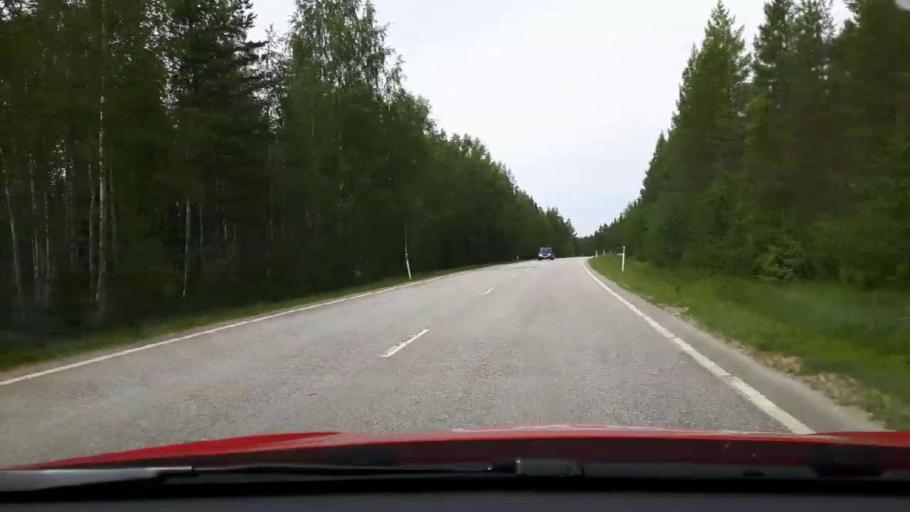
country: SE
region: Jaemtland
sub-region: Harjedalens Kommun
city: Sveg
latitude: 62.1032
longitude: 14.2069
